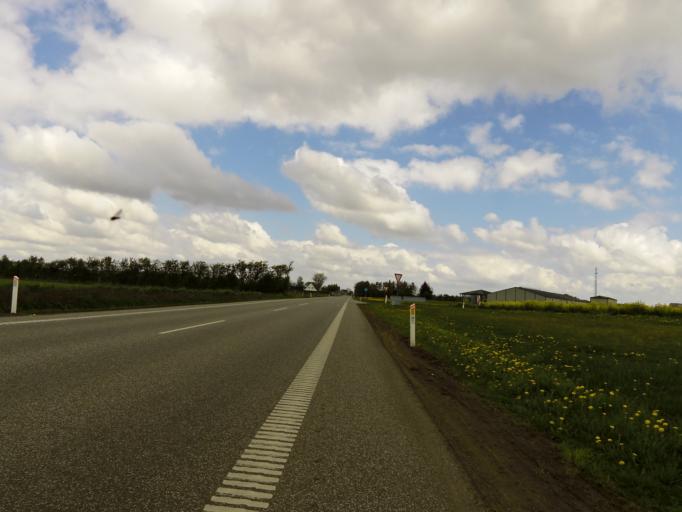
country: DK
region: South Denmark
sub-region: Haderslev Kommune
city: Gram
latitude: 55.2799
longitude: 9.0306
